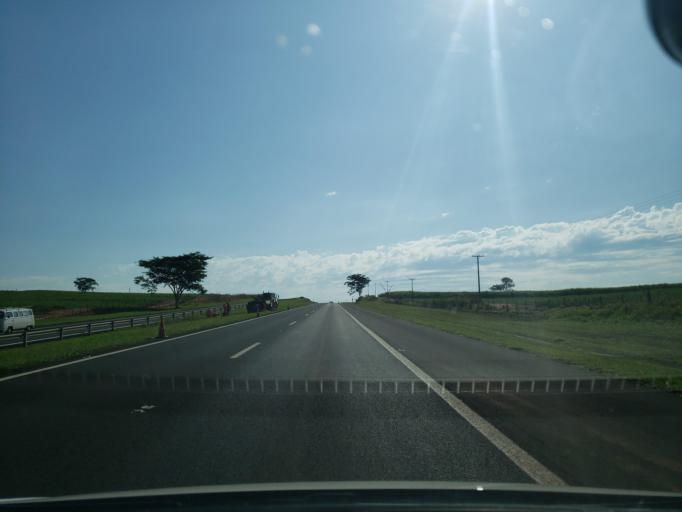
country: BR
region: Sao Paulo
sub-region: Promissao
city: Promissao
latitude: -21.5260
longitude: -49.9917
